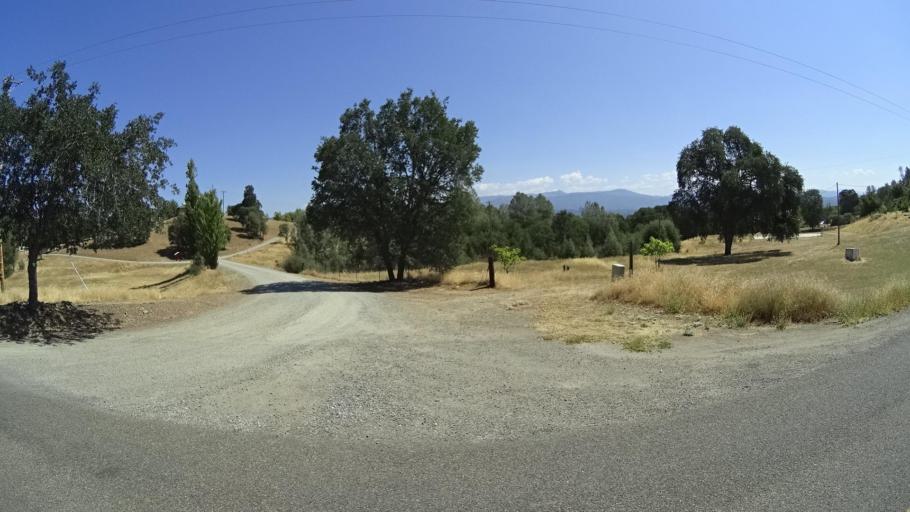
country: US
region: California
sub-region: Mariposa County
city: Mariposa
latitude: 37.4544
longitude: -119.9100
